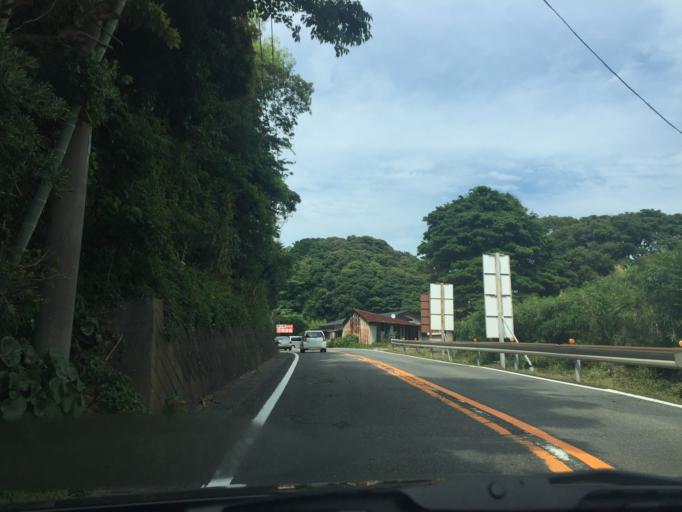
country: JP
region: Shizuoka
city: Shimoda
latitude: 34.7536
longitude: 139.0073
